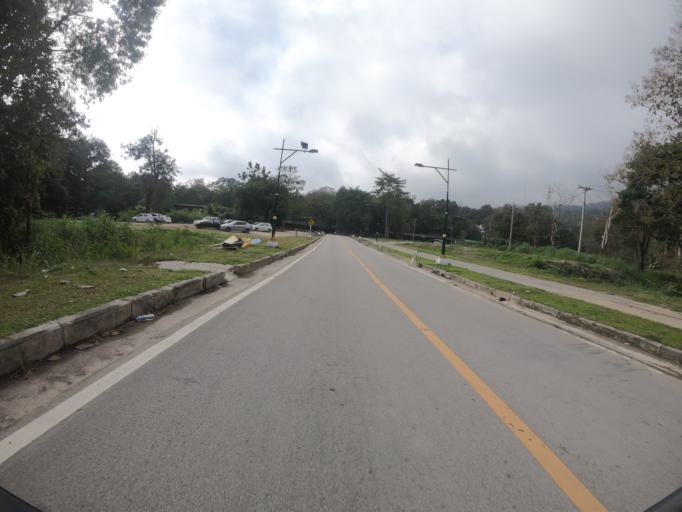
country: TH
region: Chiang Mai
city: Chiang Mai
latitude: 18.8007
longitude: 98.9484
